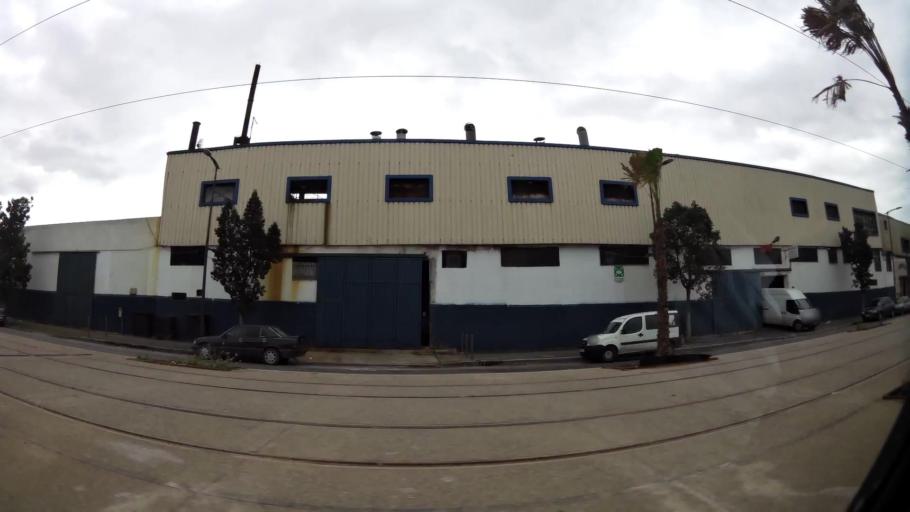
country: MA
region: Grand Casablanca
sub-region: Casablanca
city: Casablanca
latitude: 33.5760
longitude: -7.5756
